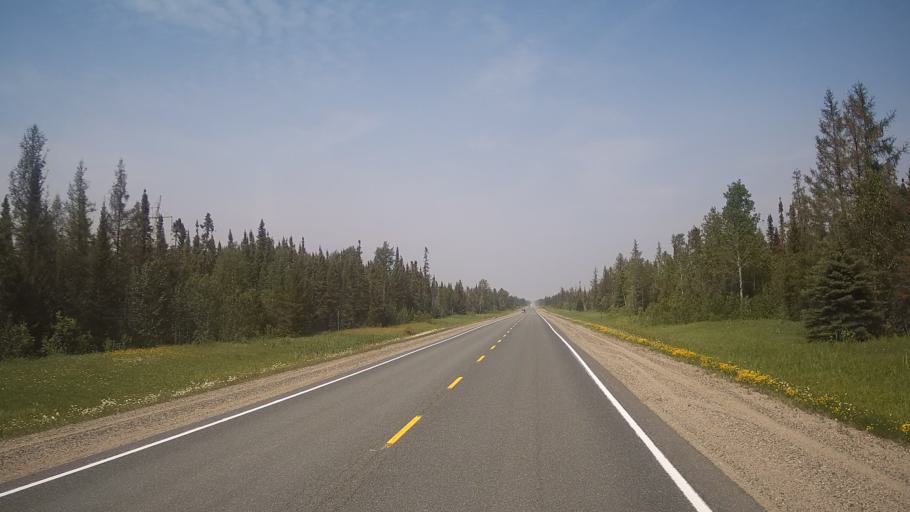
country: CA
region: Ontario
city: Timmins
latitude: 48.7840
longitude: -81.3648
